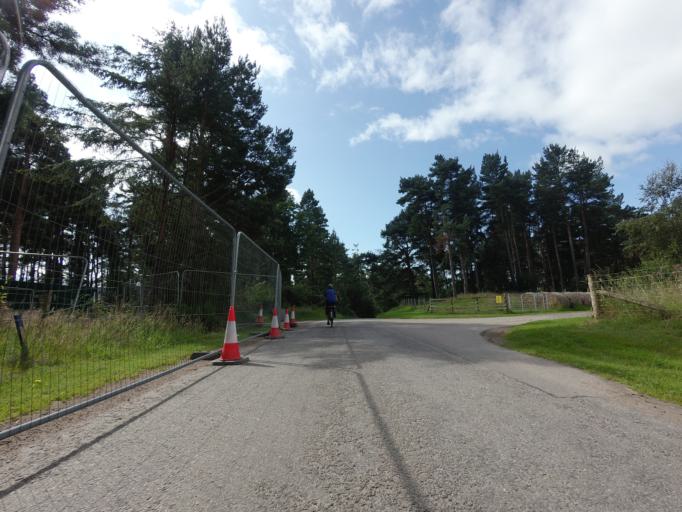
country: GB
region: Scotland
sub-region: Highland
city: Nairn
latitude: 57.5574
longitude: -3.8660
